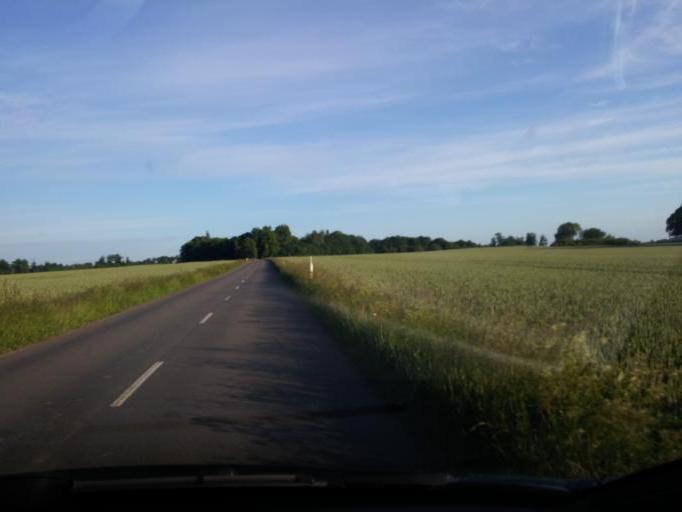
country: DK
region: South Denmark
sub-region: Kerteminde Kommune
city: Munkebo
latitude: 55.4237
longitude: 10.5449
